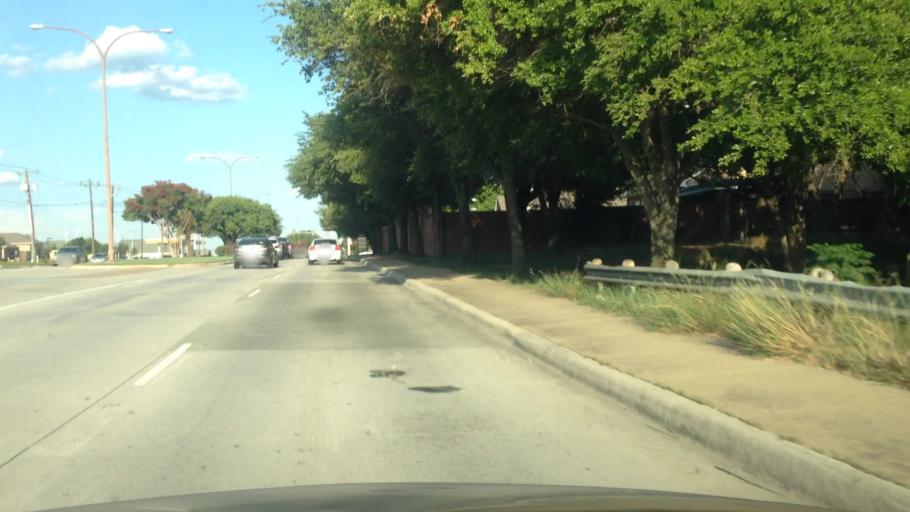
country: US
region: Texas
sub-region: Tarrant County
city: Blue Mound
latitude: 32.8609
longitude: -97.3075
